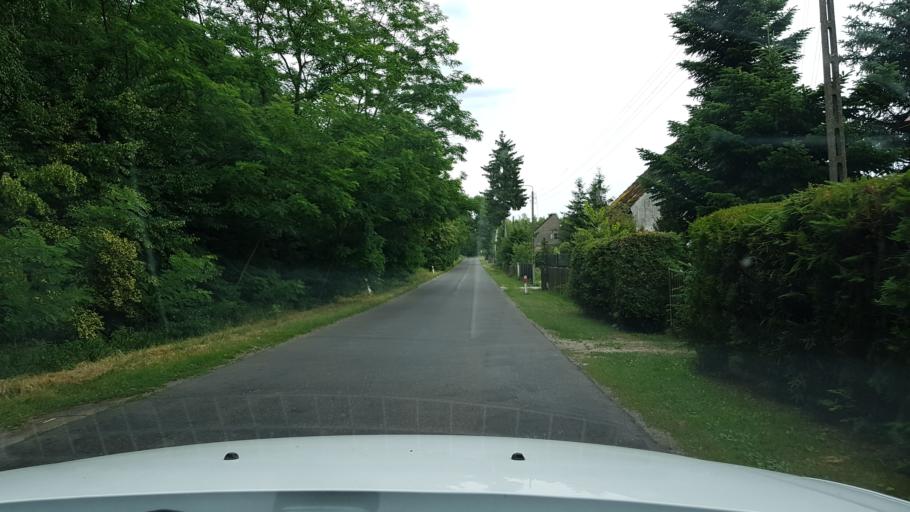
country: PL
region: West Pomeranian Voivodeship
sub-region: Powiat mysliborski
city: Boleszkowice
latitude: 52.6823
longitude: 14.6103
